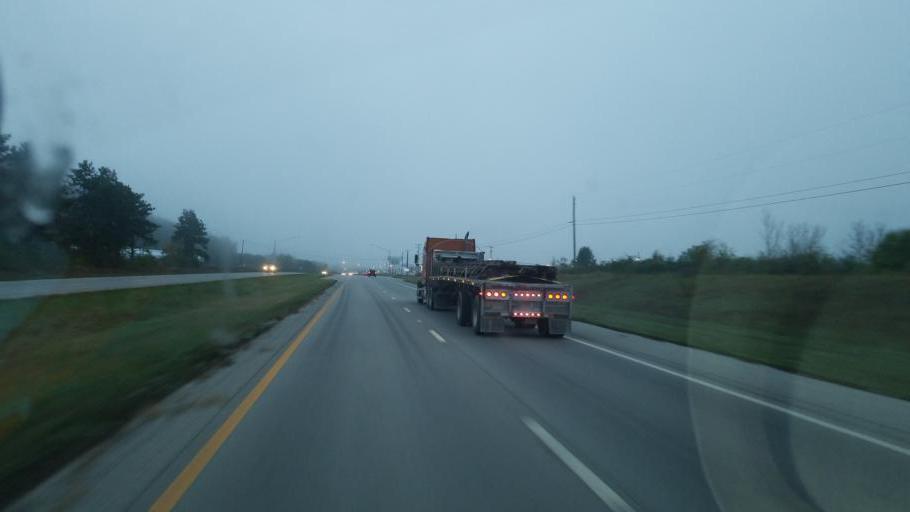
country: US
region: Ohio
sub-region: Pike County
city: Piketon
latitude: 39.0251
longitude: -83.0269
